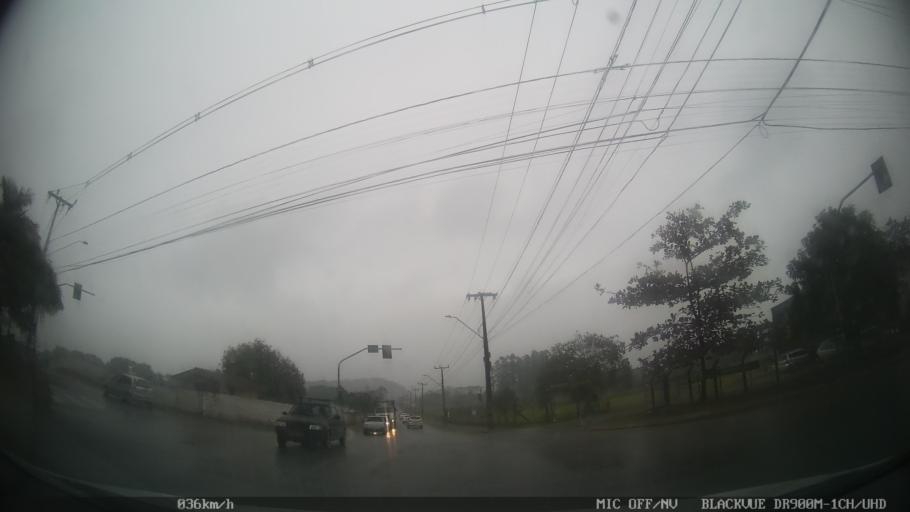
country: BR
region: Santa Catarina
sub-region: Joinville
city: Joinville
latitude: -26.2275
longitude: -48.8187
